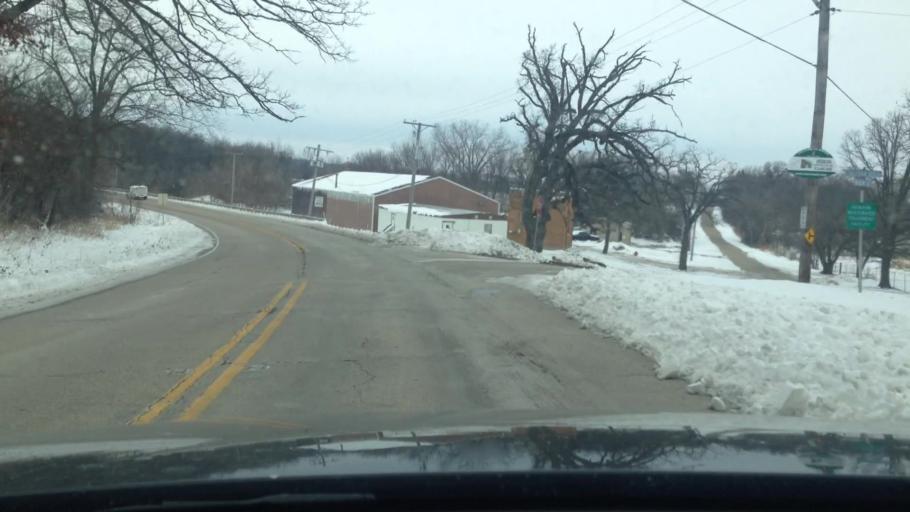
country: US
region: Illinois
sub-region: McHenry County
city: Hebron
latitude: 42.4752
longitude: -88.4329
